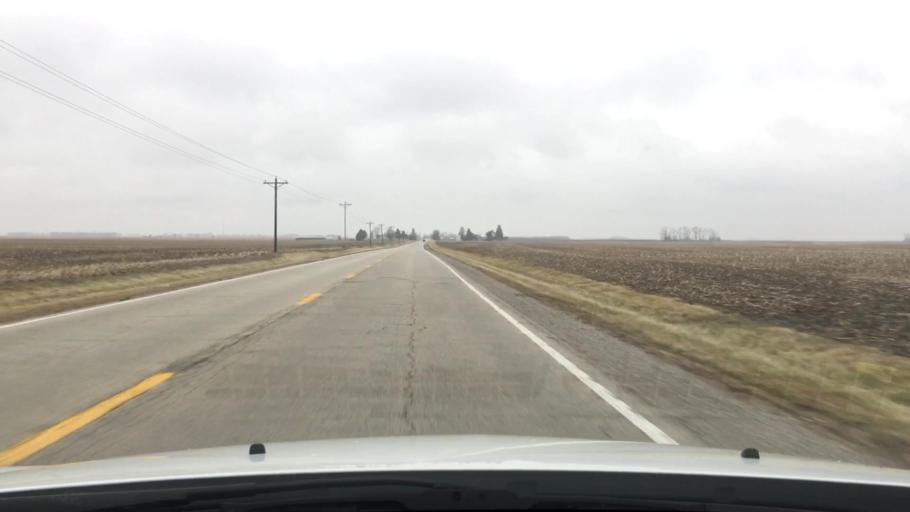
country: US
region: Illinois
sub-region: Iroquois County
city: Watseka
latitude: 40.8906
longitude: -87.6932
